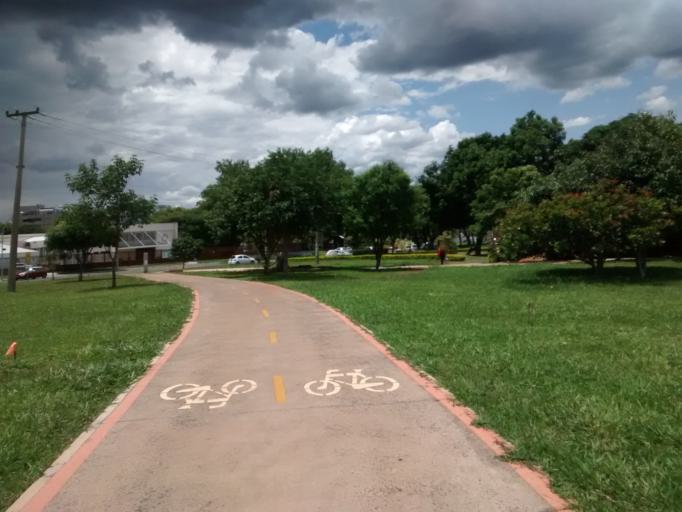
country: BR
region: Federal District
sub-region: Brasilia
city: Brasilia
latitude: -15.7598
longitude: -47.8881
